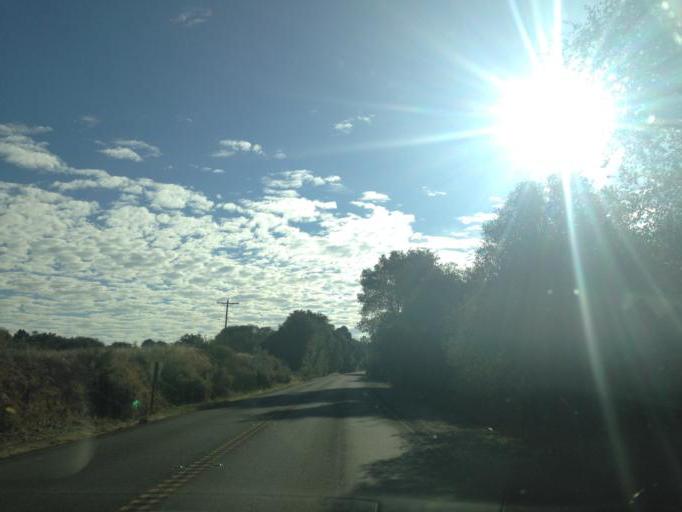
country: US
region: California
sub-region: San Diego County
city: Ramona
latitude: 33.2385
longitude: -116.7679
